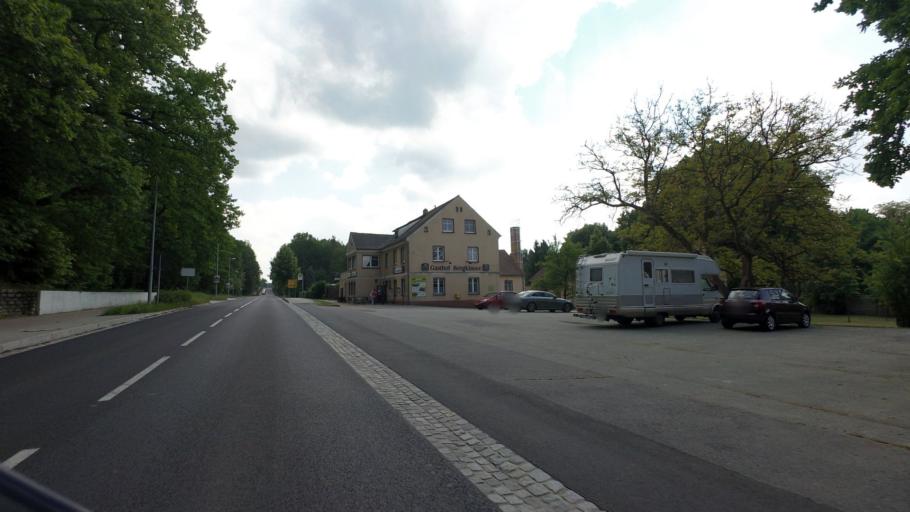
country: DE
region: Saxony
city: Rietschen
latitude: 51.3884
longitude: 14.7853
